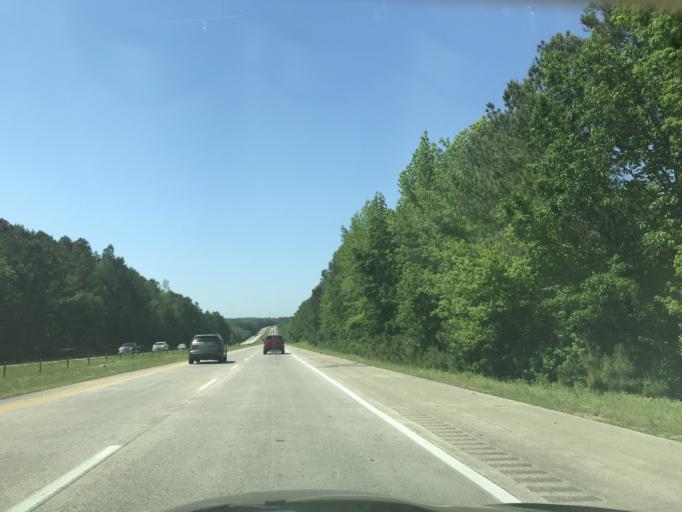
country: US
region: North Carolina
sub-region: Johnston County
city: Benson
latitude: 35.4554
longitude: -78.5360
